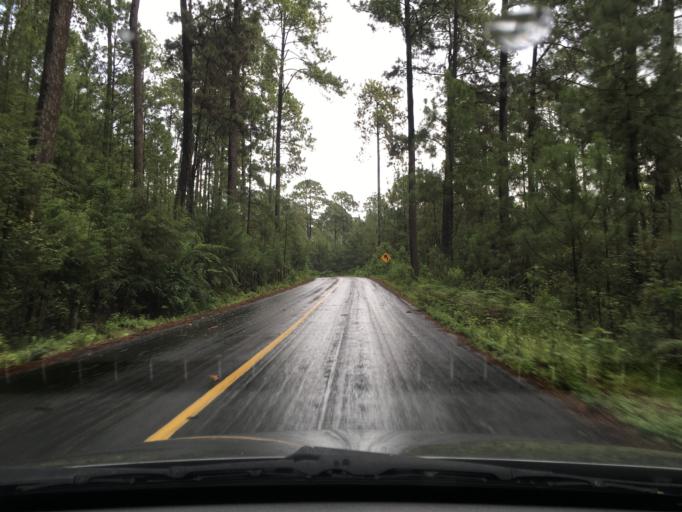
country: MX
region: Michoacan
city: Nuevo San Juan Parangaricutiro
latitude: 19.4386
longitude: -102.1500
